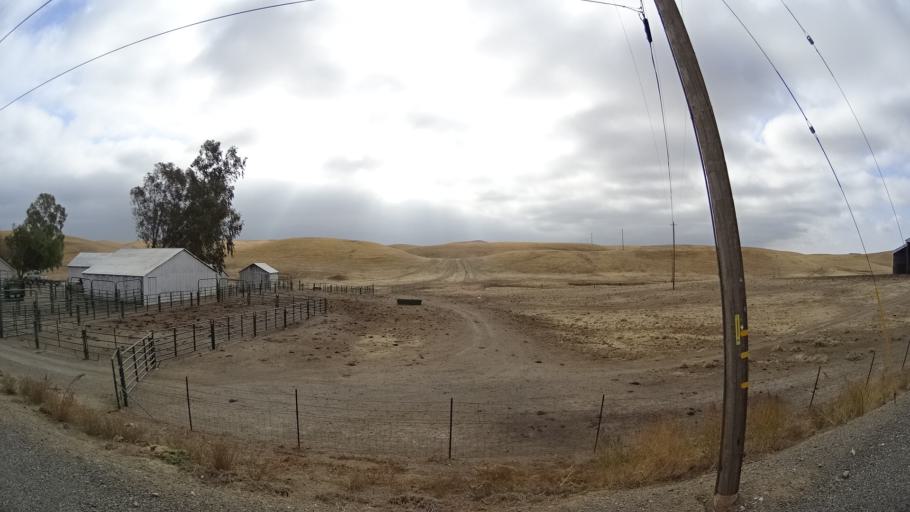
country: US
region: California
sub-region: Yolo County
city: Dunnigan
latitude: 38.7845
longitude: -121.9236
